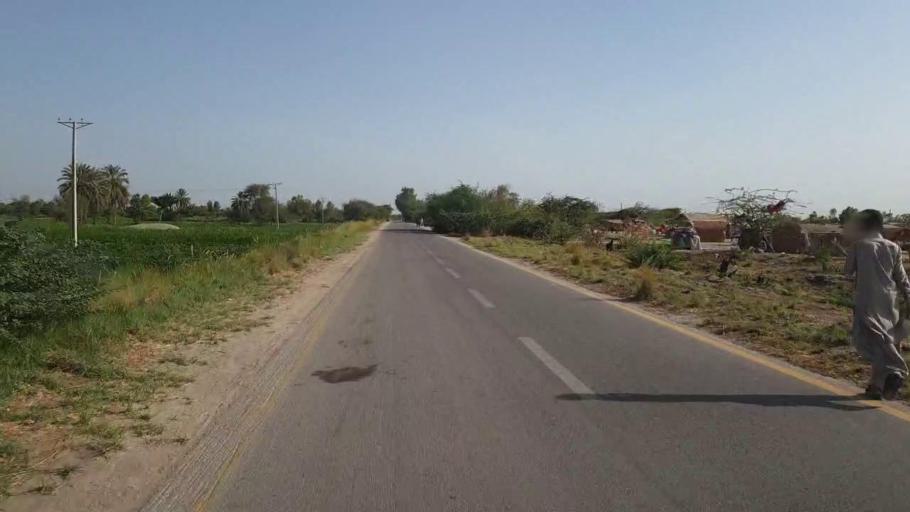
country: PK
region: Sindh
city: Daur
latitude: 26.4646
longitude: 68.4519
